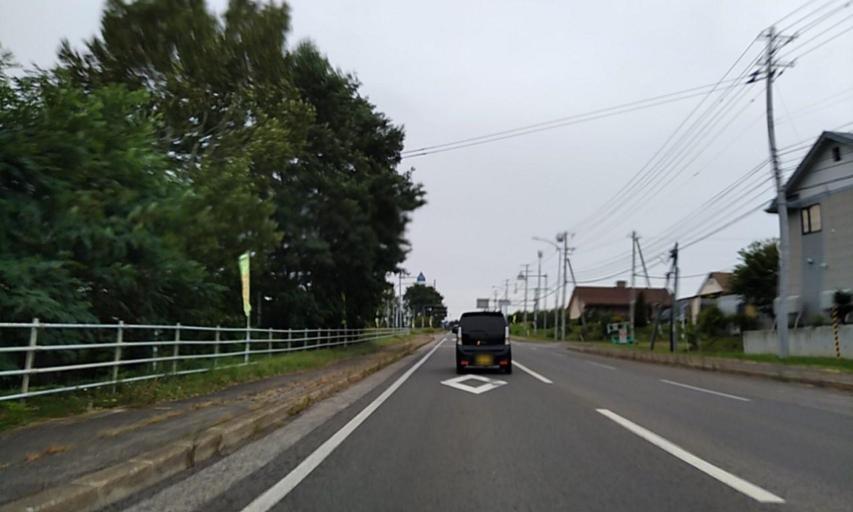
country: JP
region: Hokkaido
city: Bihoro
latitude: 43.9138
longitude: 144.1839
